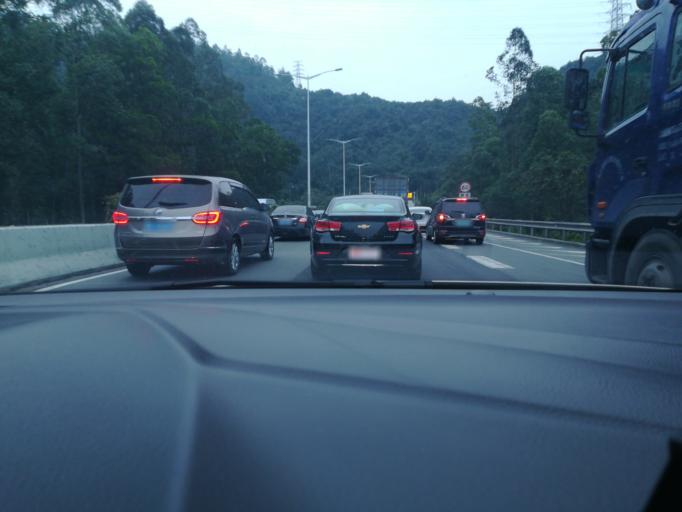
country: CN
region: Guangdong
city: Longdong
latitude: 23.2265
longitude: 113.3561
